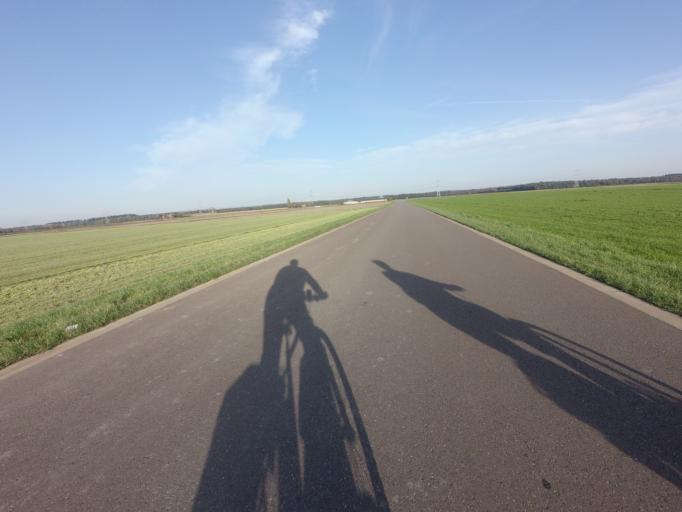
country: NL
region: Limburg
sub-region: Gemeente Roerdalen
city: Montfort
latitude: 51.1126
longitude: 5.9705
